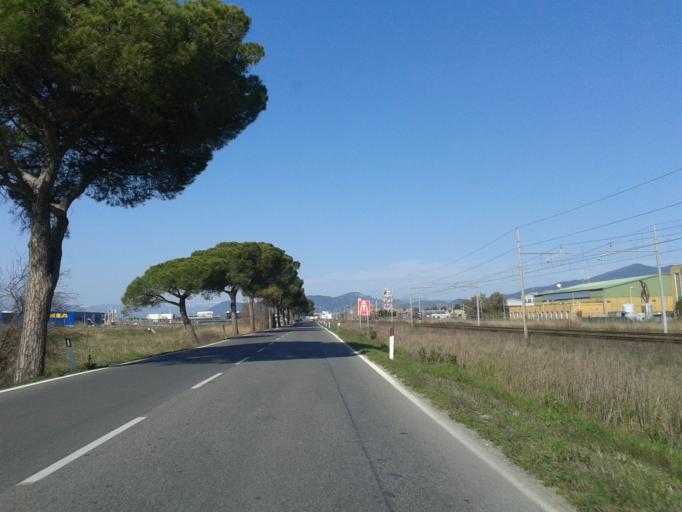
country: IT
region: Tuscany
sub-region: Province of Pisa
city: Pisa
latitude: 43.6870
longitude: 10.3834
